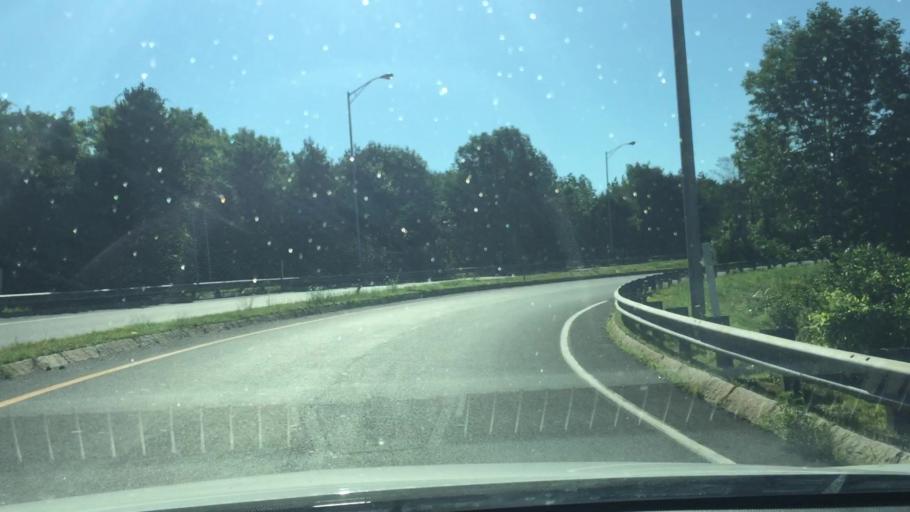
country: US
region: Massachusetts
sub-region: Berkshire County
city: Lee
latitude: 42.3000
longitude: -73.2342
